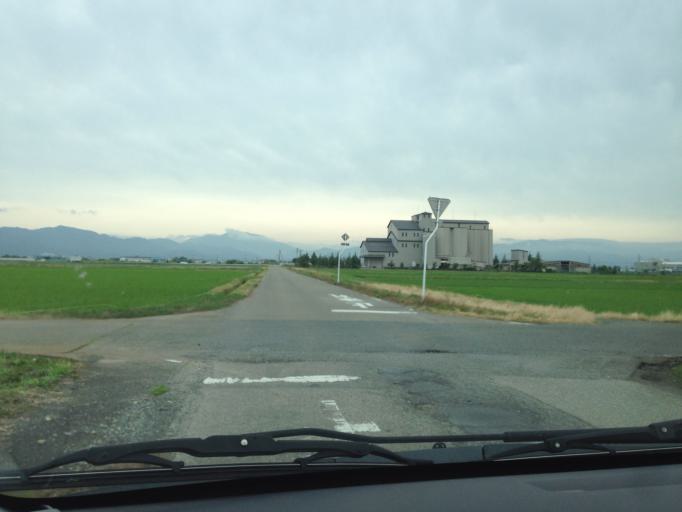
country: JP
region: Fukushima
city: Kitakata
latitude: 37.5336
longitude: 139.8928
